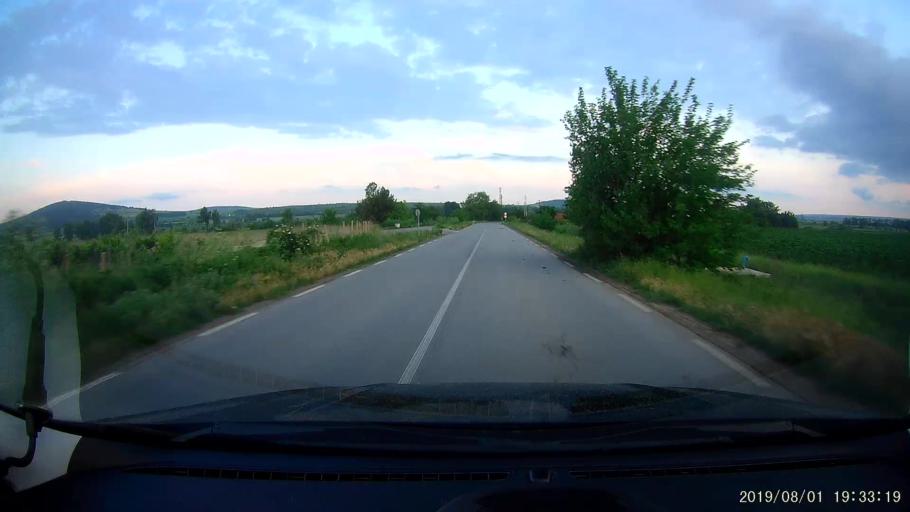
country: BG
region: Burgas
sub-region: Obshtina Sungurlare
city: Sungurlare
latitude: 42.7817
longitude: 26.8759
